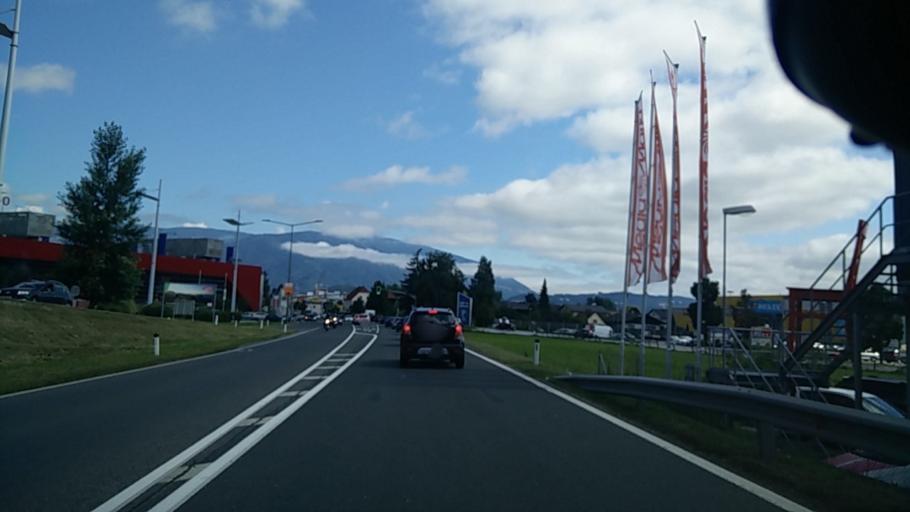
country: AT
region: Carinthia
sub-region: Villach Stadt
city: Villach
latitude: 46.5940
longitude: 13.8364
